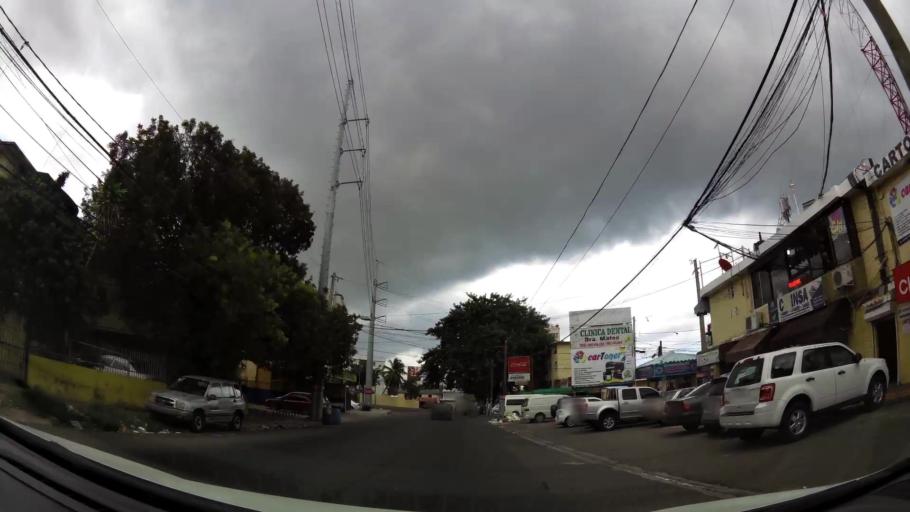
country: DO
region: Nacional
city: La Julia
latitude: 18.4568
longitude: -69.9276
